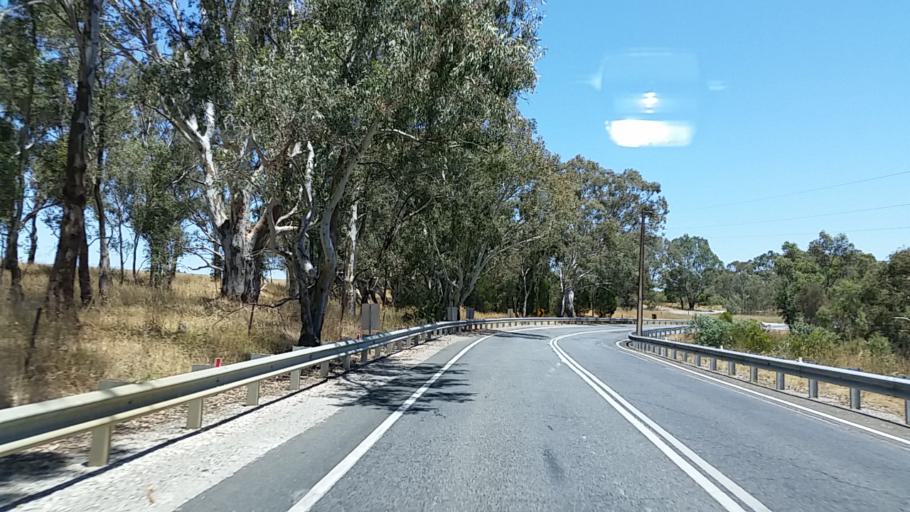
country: AU
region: South Australia
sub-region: Adelaide Hills
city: Birdwood
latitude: -34.8020
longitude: 138.9982
